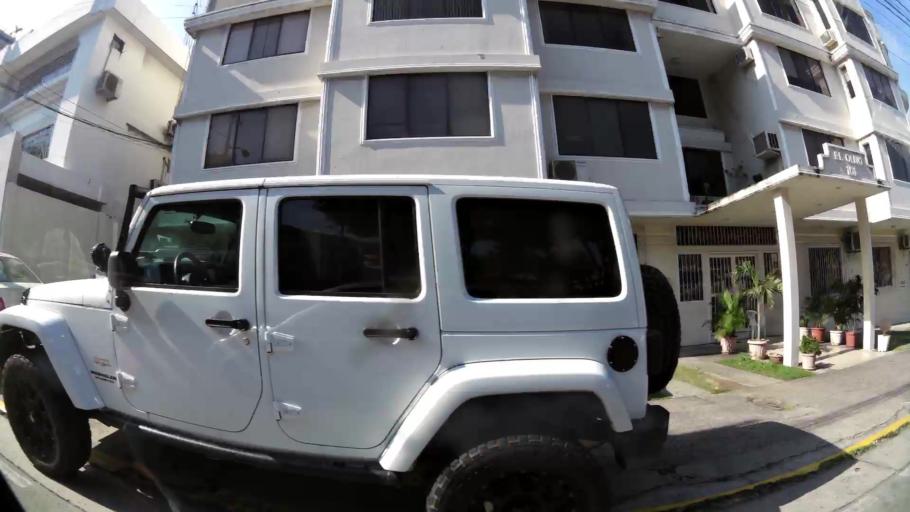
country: EC
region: Guayas
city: Guayaquil
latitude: -2.1708
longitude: -79.9429
